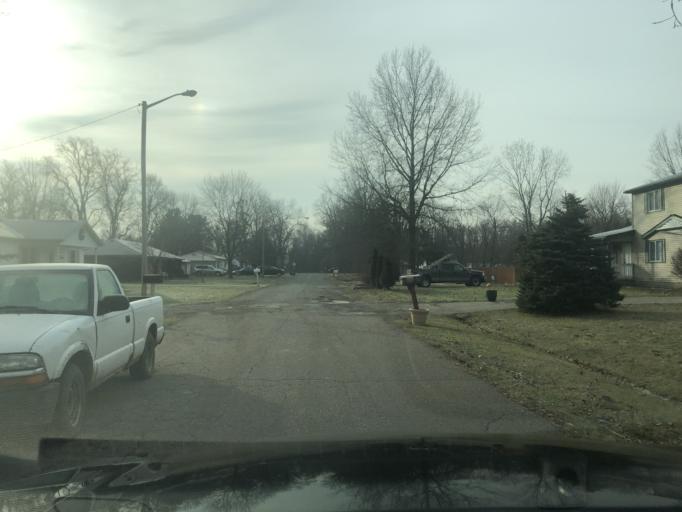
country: US
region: Michigan
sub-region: Wayne County
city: Romulus
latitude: 42.1871
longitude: -83.3269
